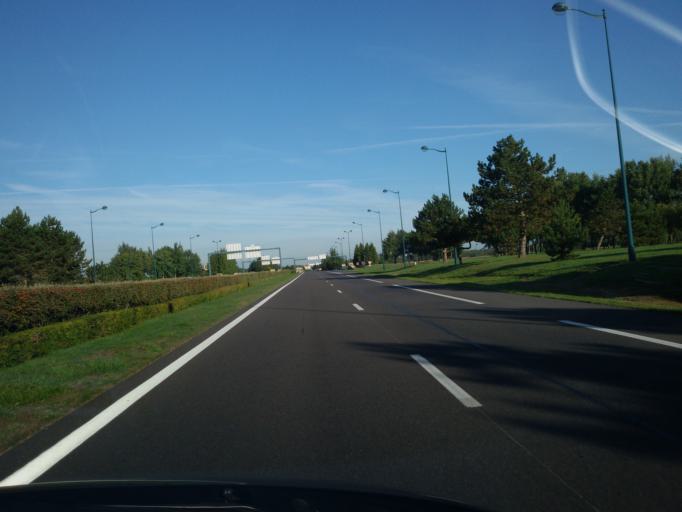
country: FR
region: Ile-de-France
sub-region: Departement de Seine-et-Marne
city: Magny-le-Hongre
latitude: 48.8530
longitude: 2.8025
